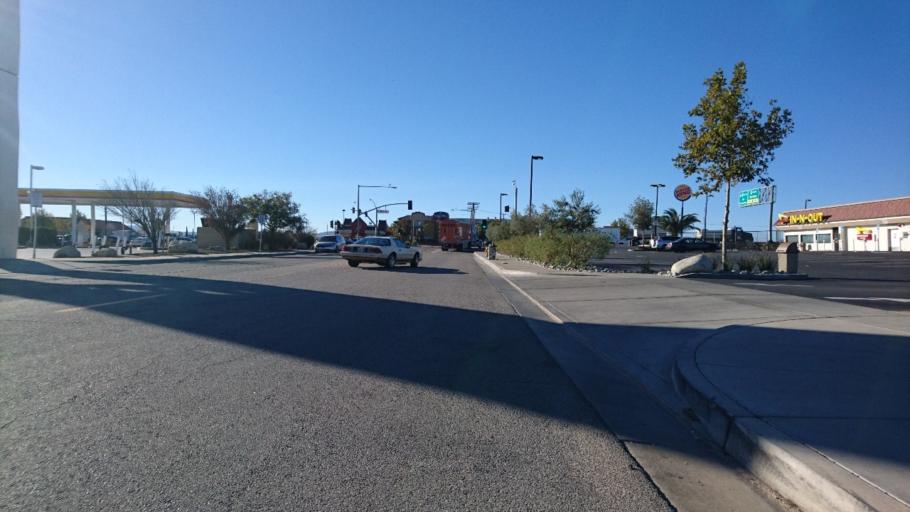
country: US
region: California
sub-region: San Bernardino County
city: Oak Hills
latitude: 34.4278
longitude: -117.3777
